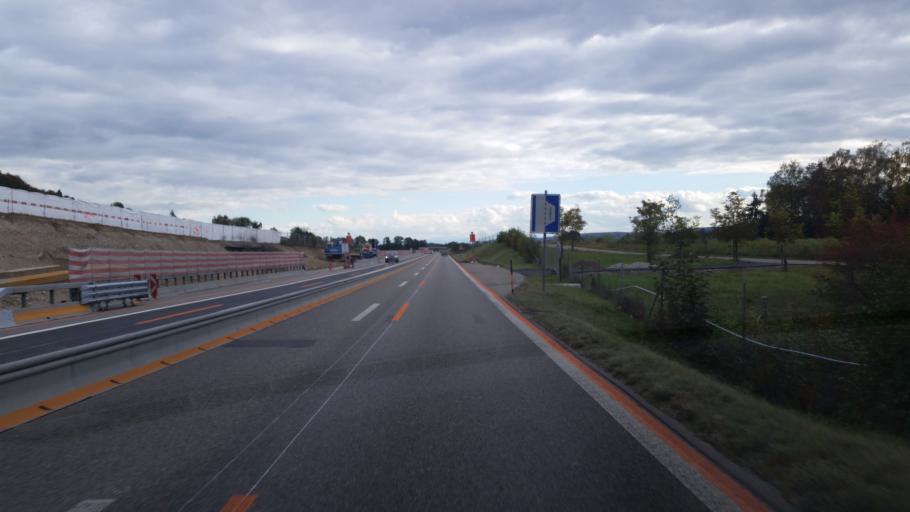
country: CH
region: Zurich
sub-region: Bezirk Buelach
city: Bachenbulach
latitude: 47.4880
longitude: 8.5437
